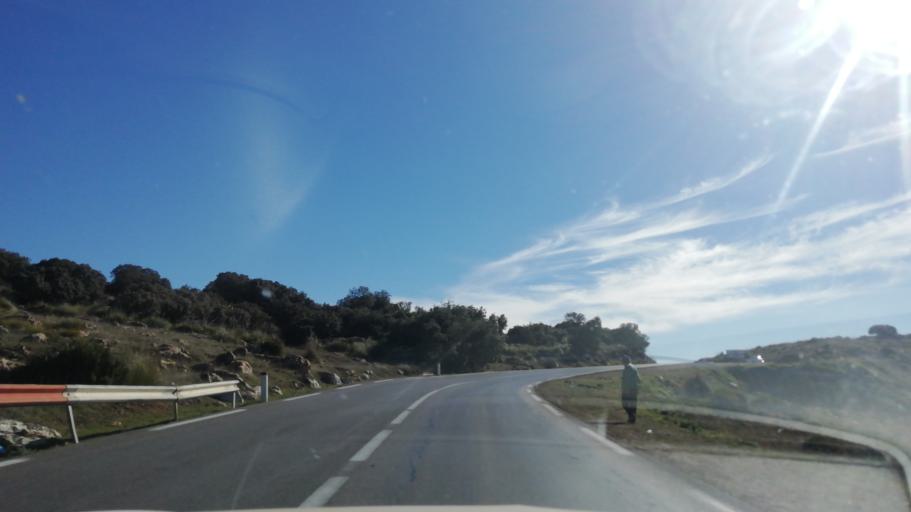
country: DZ
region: Tlemcen
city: Mansoura
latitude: 34.8273
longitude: -1.3690
